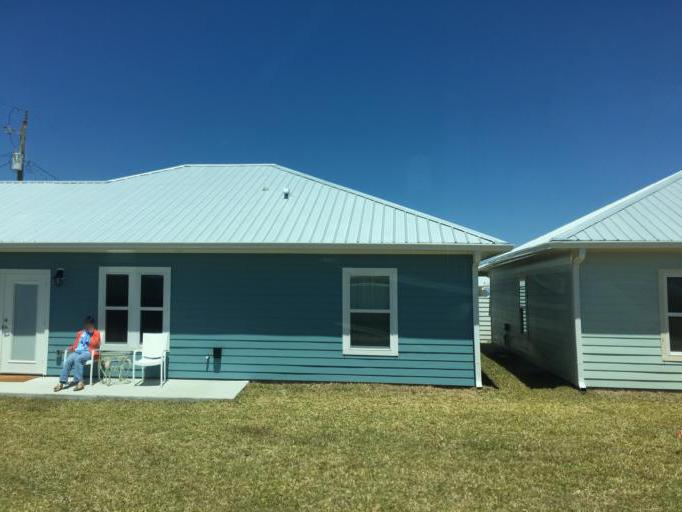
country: US
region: Florida
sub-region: Bay County
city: Laguna Beach
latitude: 30.2421
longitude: -85.9249
